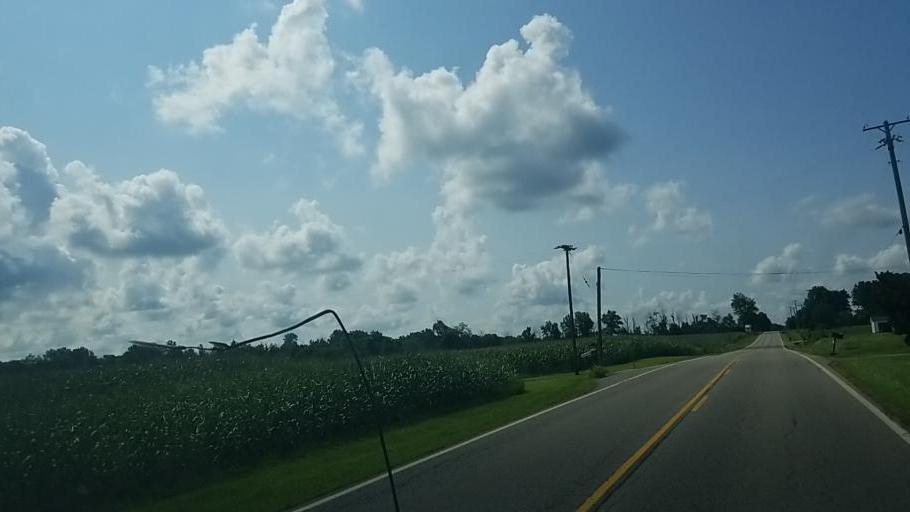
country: US
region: Ohio
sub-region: Ashland County
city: Ashland
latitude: 40.7661
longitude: -82.3068
